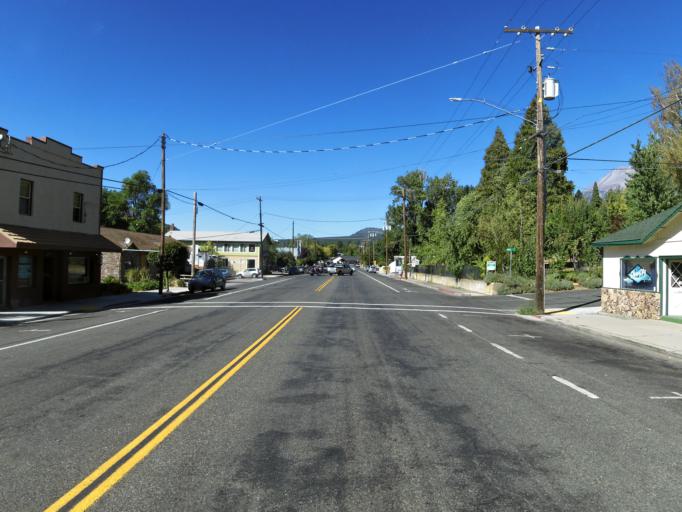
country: US
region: California
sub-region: Siskiyou County
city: Mount Shasta
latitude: 41.3102
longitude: -122.3110
